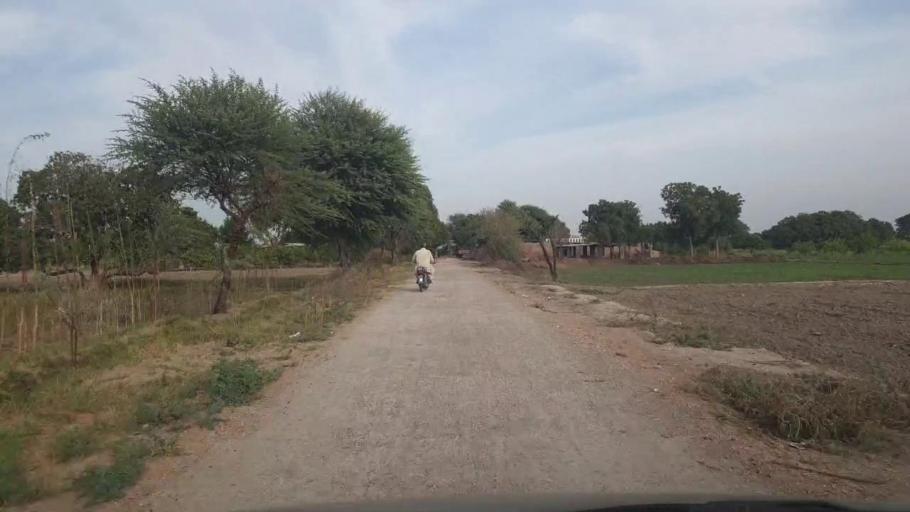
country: PK
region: Sindh
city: Kunri
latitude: 25.2732
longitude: 69.5706
